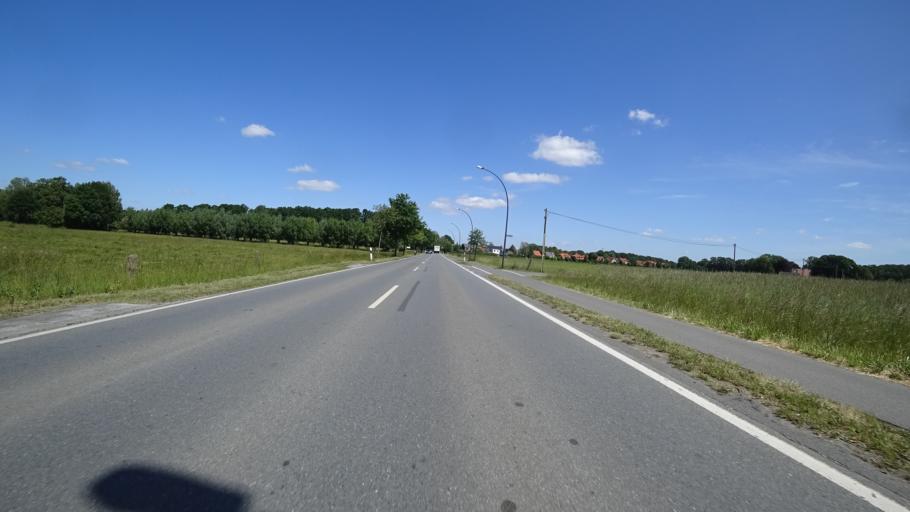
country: DE
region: North Rhine-Westphalia
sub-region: Regierungsbezirk Detmold
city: Guetersloh
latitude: 51.9165
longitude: 8.4279
